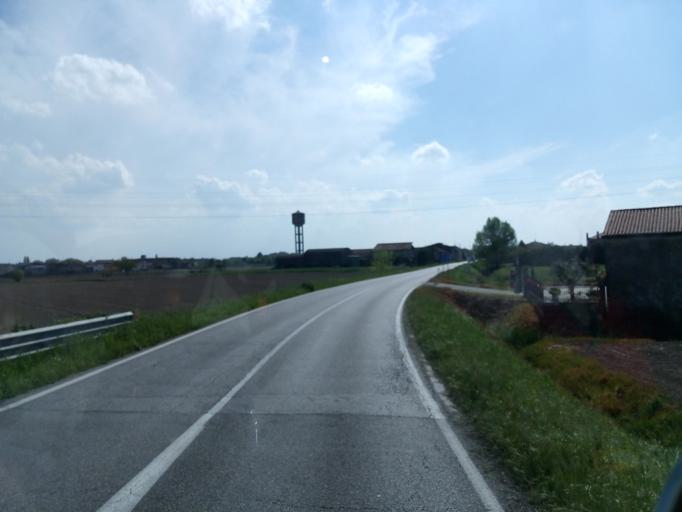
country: IT
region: Veneto
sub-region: Provincia di Verona
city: Boschi Sant'Anna
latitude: 45.2092
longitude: 11.3195
